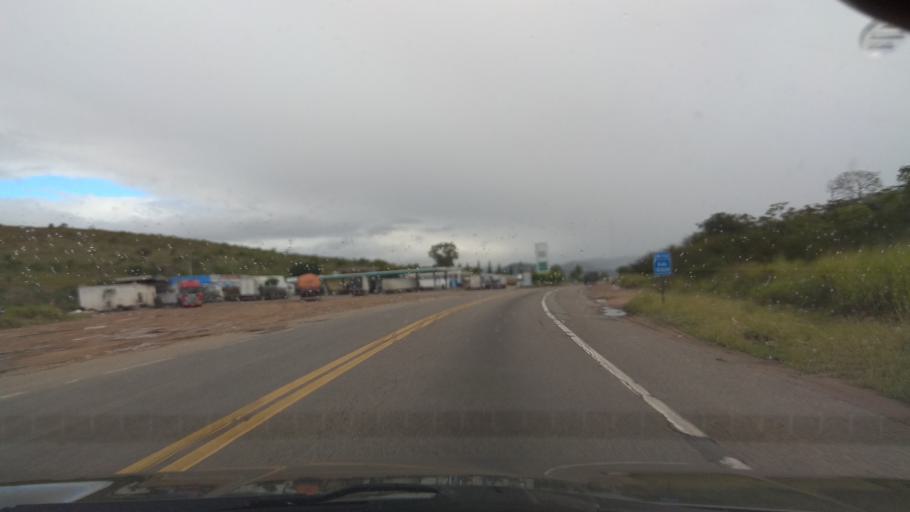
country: BR
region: Bahia
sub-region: Amargosa
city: Amargosa
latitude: -12.9035
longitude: -39.8612
